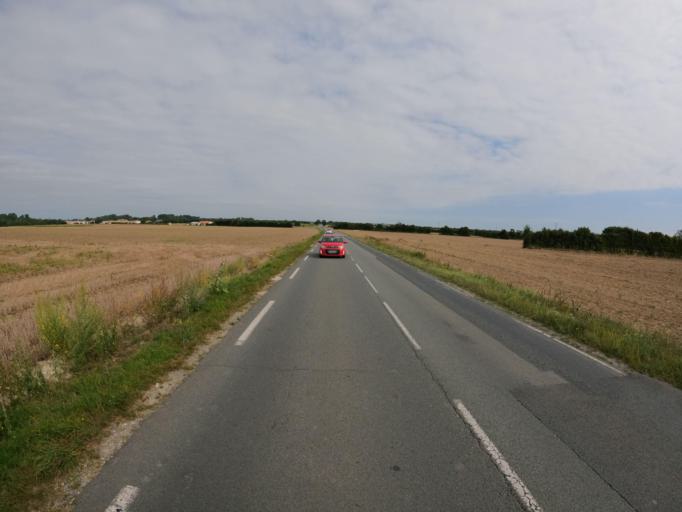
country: FR
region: Poitou-Charentes
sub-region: Departement de la Charente-Maritime
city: Saint-Jean-de-Liversay
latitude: 46.2466
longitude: -0.8814
